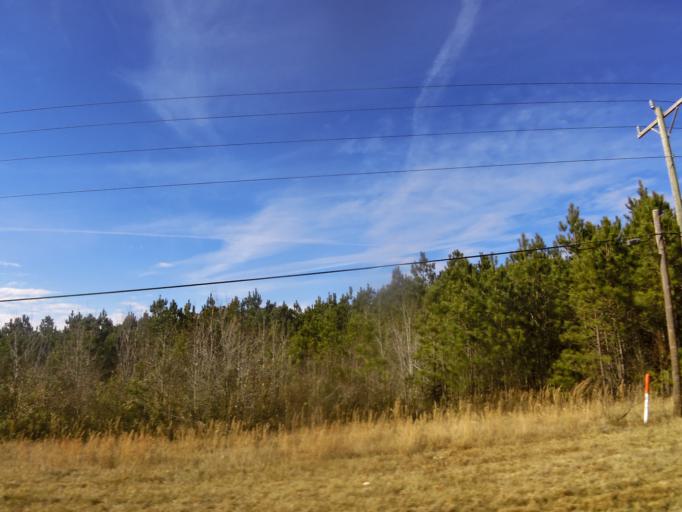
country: US
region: Virginia
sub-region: Isle of Wight County
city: Windsor
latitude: 36.7971
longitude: -76.7670
